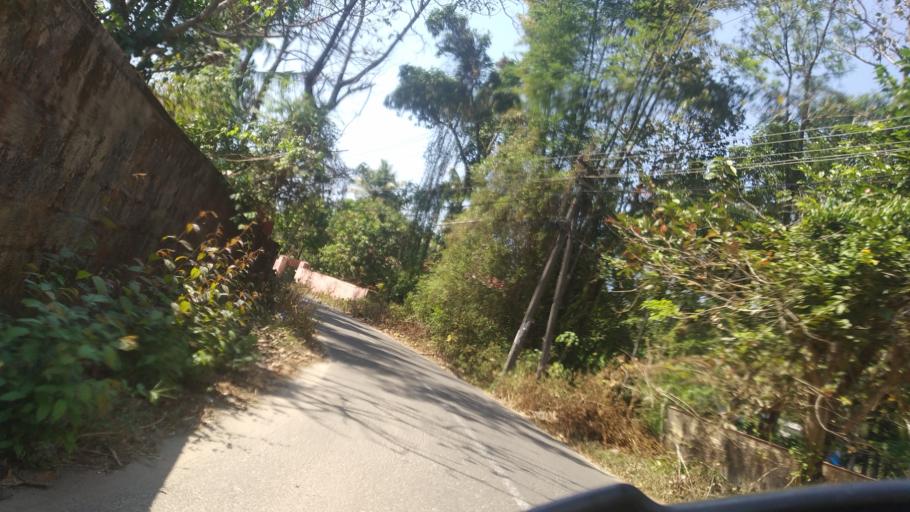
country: IN
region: Kerala
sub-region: Ernakulam
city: Elur
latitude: 10.1303
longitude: 76.2306
